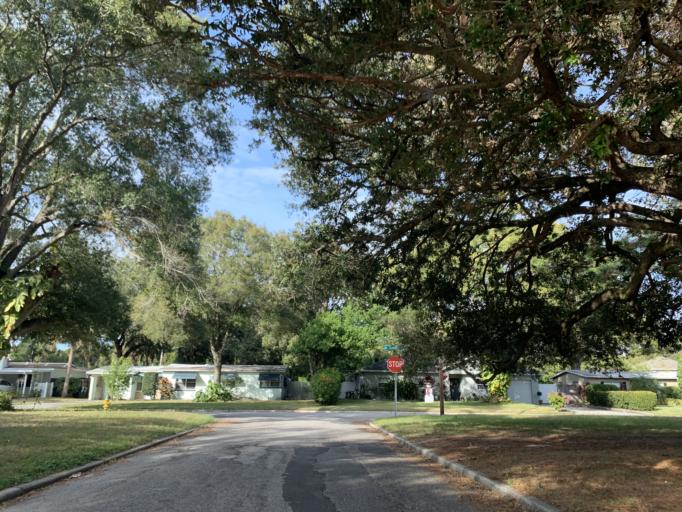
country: US
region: Florida
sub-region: Hillsborough County
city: Tampa
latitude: 27.9039
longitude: -82.5148
